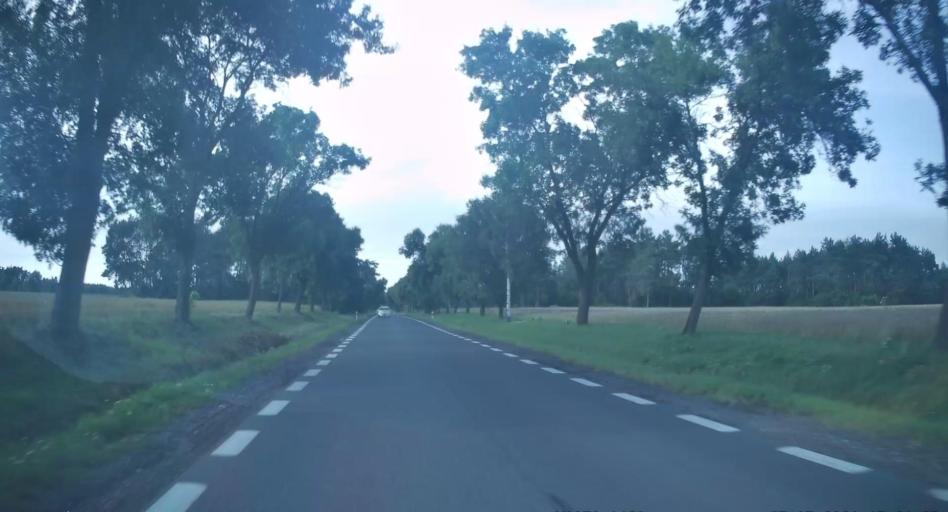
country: PL
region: Lodz Voivodeship
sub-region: Powiat tomaszowski
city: Rzeczyca
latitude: 51.6356
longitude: 20.2897
